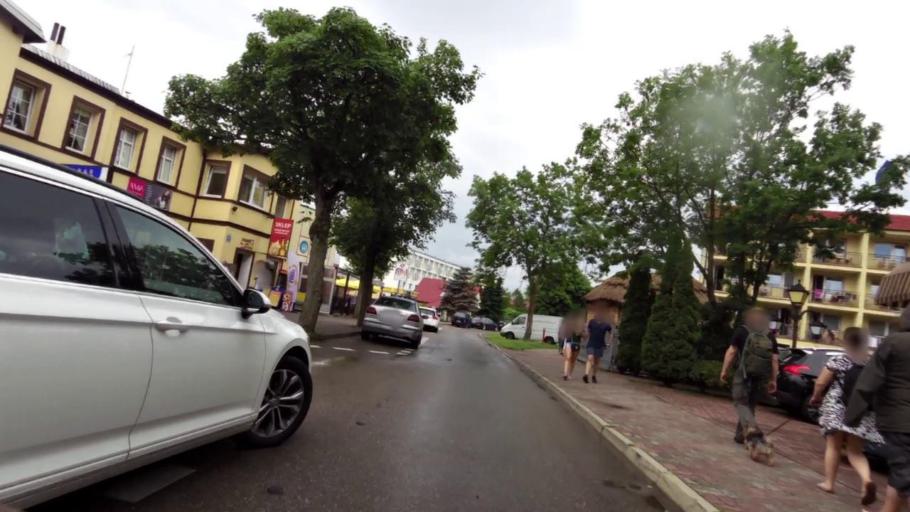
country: PL
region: West Pomeranian Voivodeship
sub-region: Powiat kolobrzeski
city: Ustronie Morskie
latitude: 54.2164
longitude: 15.7574
